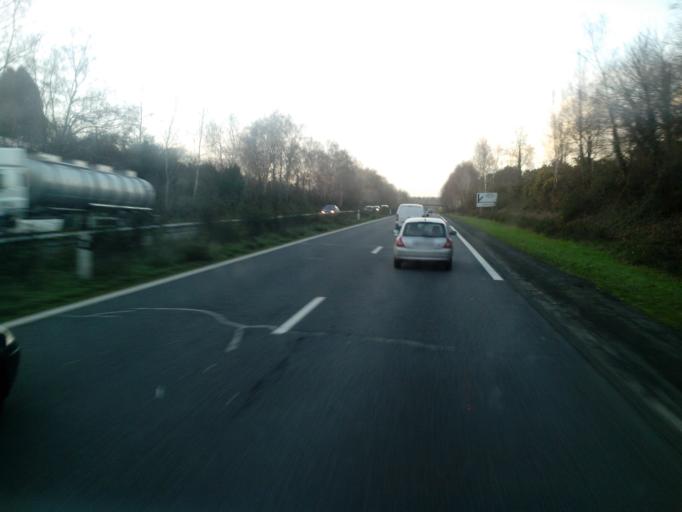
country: FR
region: Pays de la Loire
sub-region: Departement de la Loire-Atlantique
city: Haute-Goulaine
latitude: 47.1899
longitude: -1.4301
